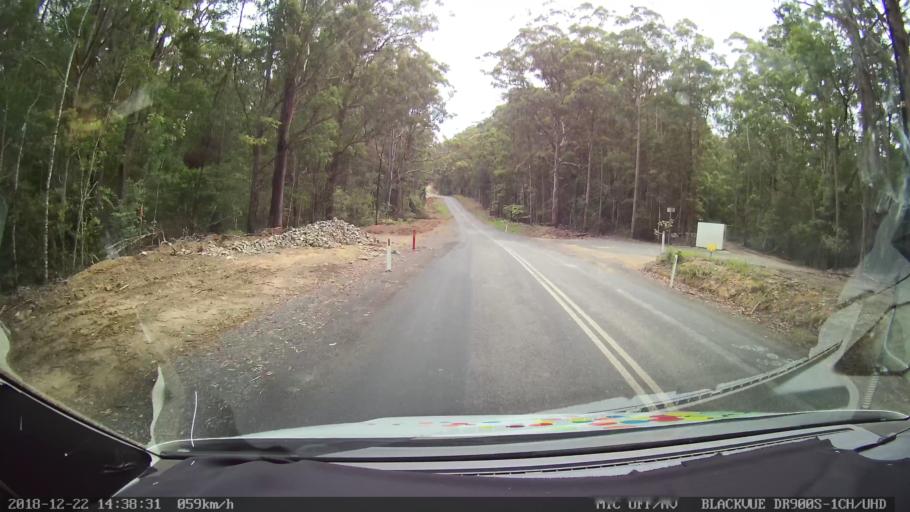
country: AU
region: New South Wales
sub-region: Bellingen
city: Dorrigo
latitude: -30.1390
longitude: 152.5972
